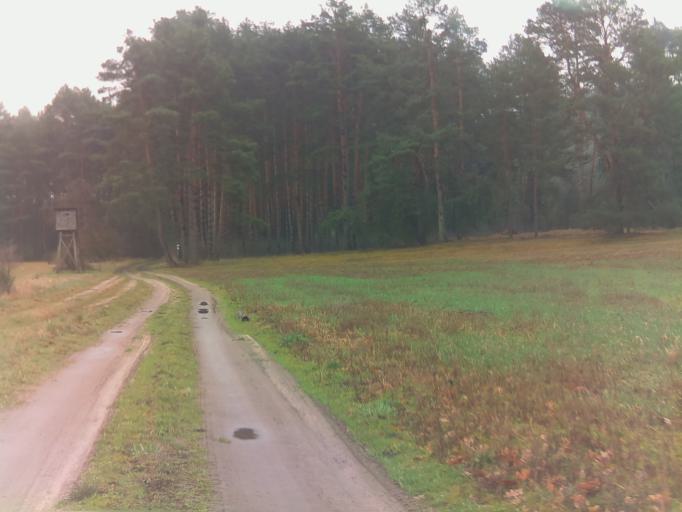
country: DE
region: Brandenburg
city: Lieberose
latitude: 52.0087
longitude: 14.2236
